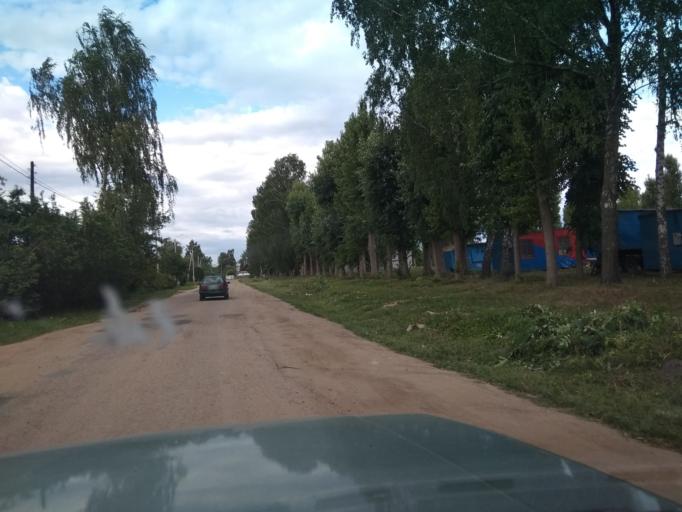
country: BY
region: Mogilev
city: Mahilyow
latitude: 53.9247
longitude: 30.3454
